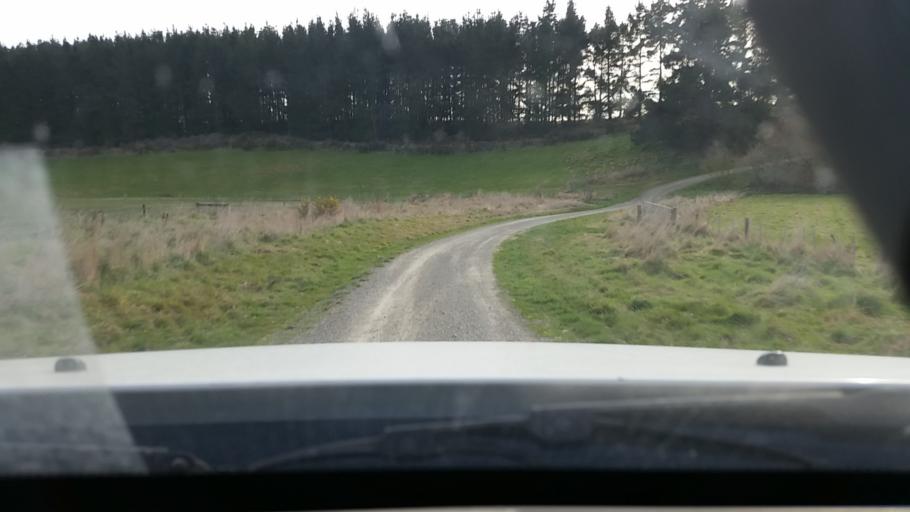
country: NZ
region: Canterbury
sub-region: Timaru District
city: Pleasant Point
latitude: -44.1970
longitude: 171.1876
